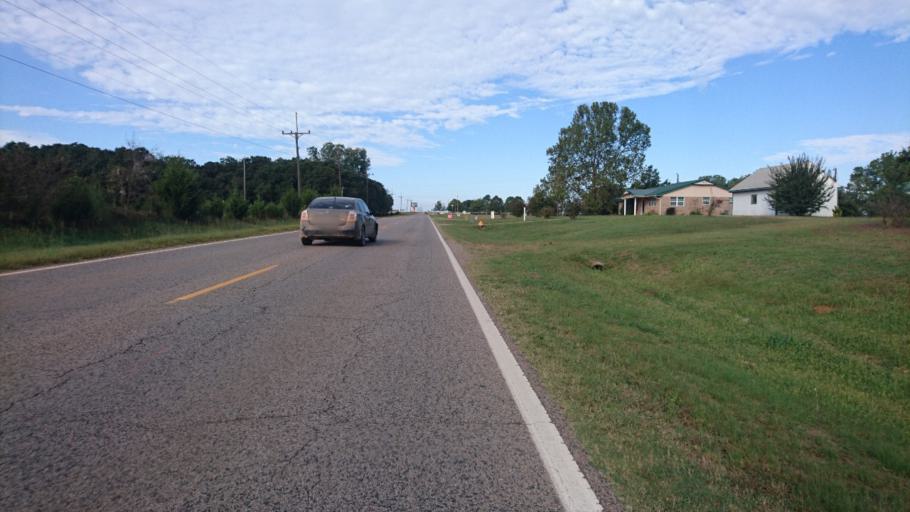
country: US
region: Oklahoma
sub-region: Lincoln County
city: Chandler
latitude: 35.6811
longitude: -97.0335
